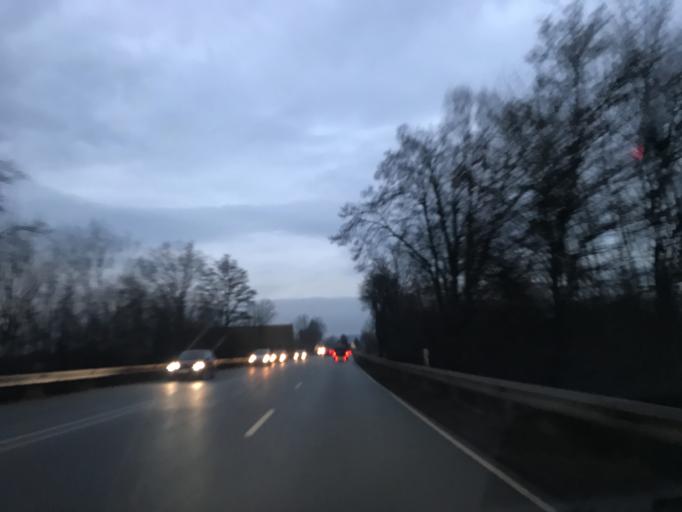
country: DE
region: Hesse
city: Grebenstein
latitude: 51.4256
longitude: 9.4363
